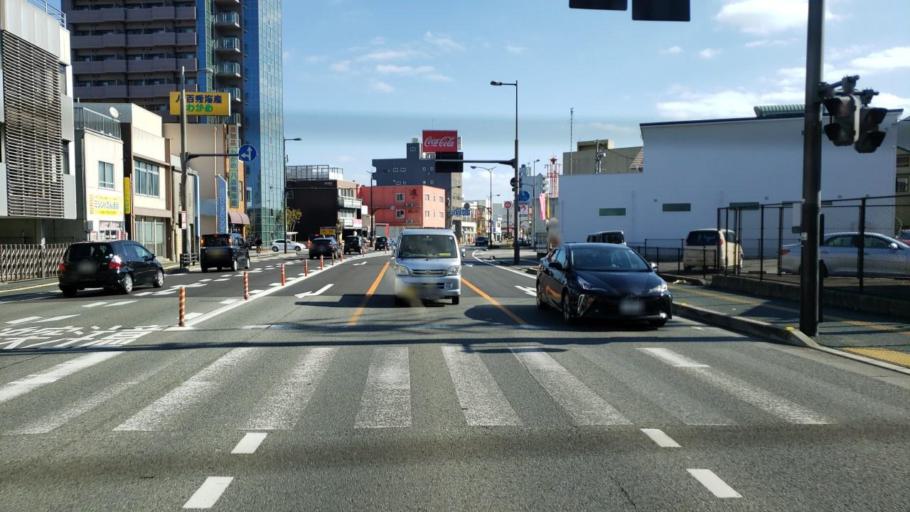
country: JP
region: Tokushima
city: Tokushima-shi
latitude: 34.0789
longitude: 134.5279
